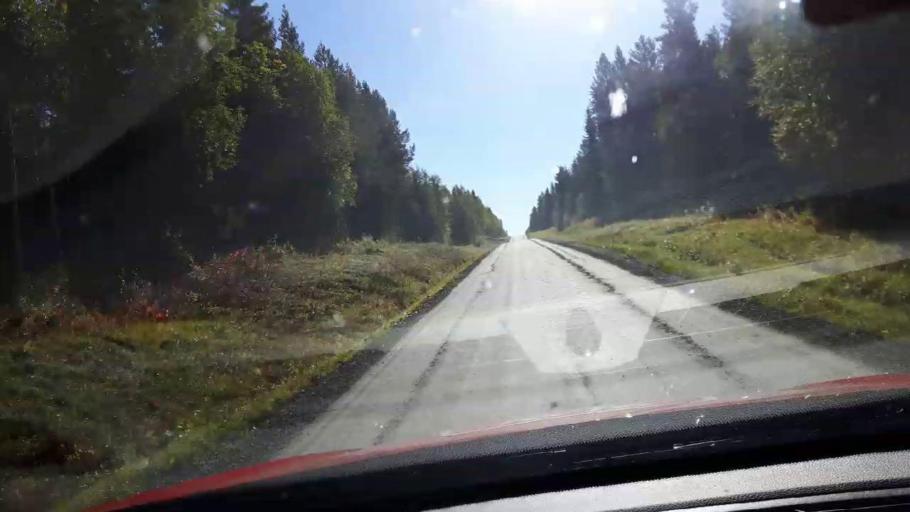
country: NO
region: Nord-Trondelag
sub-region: Lierne
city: Sandvika
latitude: 64.6079
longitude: 13.9597
